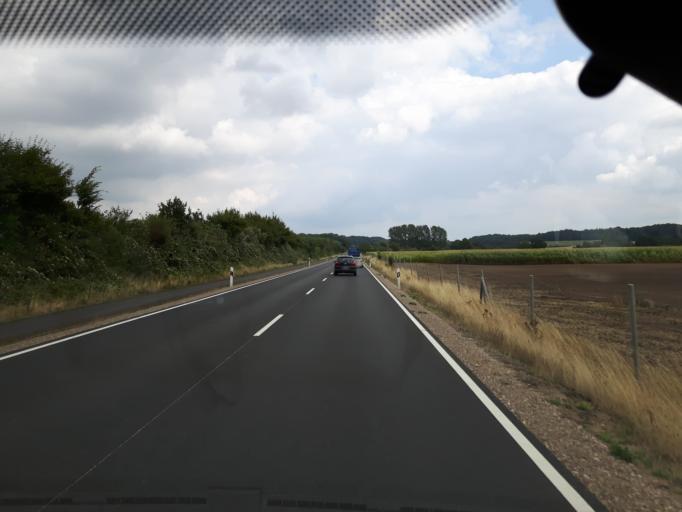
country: DE
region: Schleswig-Holstein
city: Gross Wittensee
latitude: 54.4120
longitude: 9.7760
